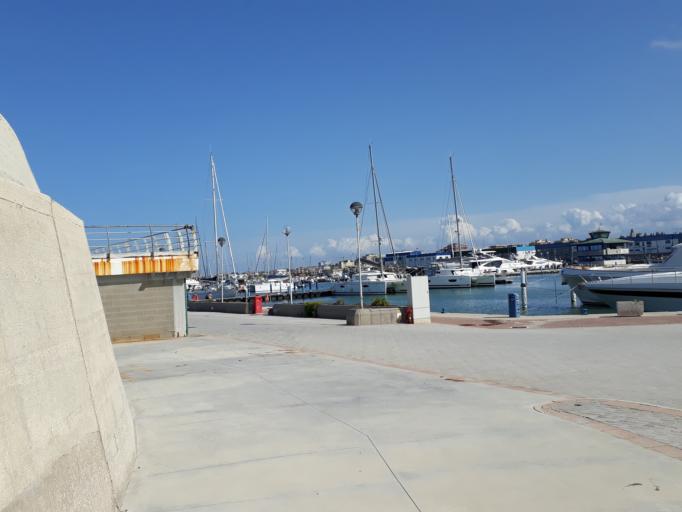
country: IT
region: The Marches
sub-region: Provincia di Pesaro e Urbino
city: Fano
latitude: 43.8552
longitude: 13.0166
